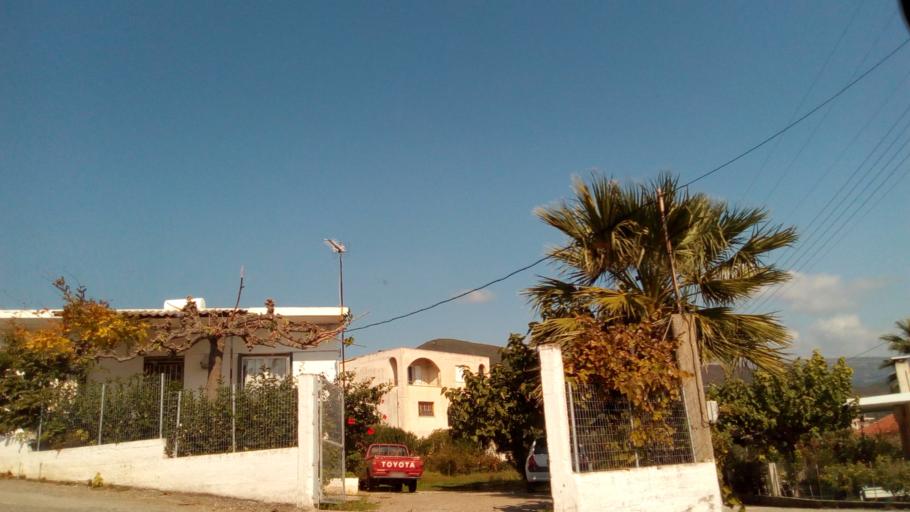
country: GR
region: West Greece
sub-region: Nomos Aitolias kai Akarnanias
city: Antirrio
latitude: 38.3657
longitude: 21.7750
